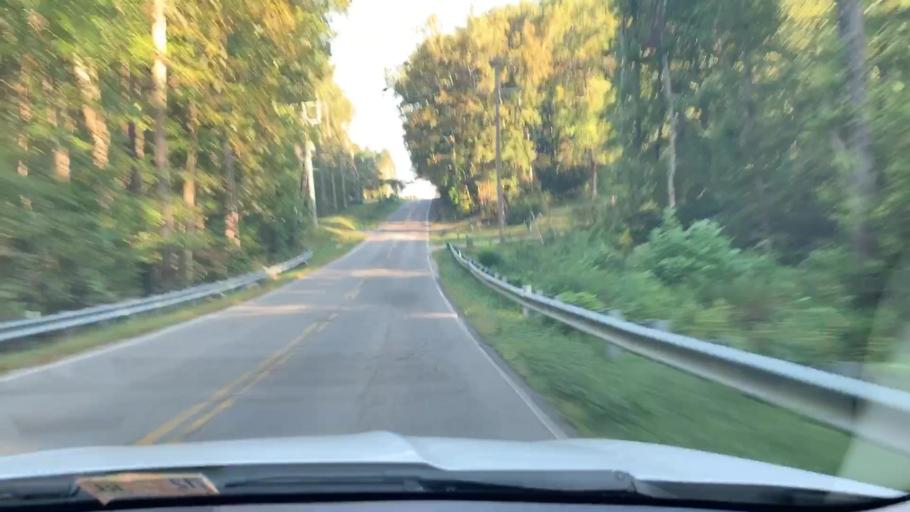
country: US
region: Virginia
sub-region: Middlesex County
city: Deltaville
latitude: 37.5656
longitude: -76.4524
